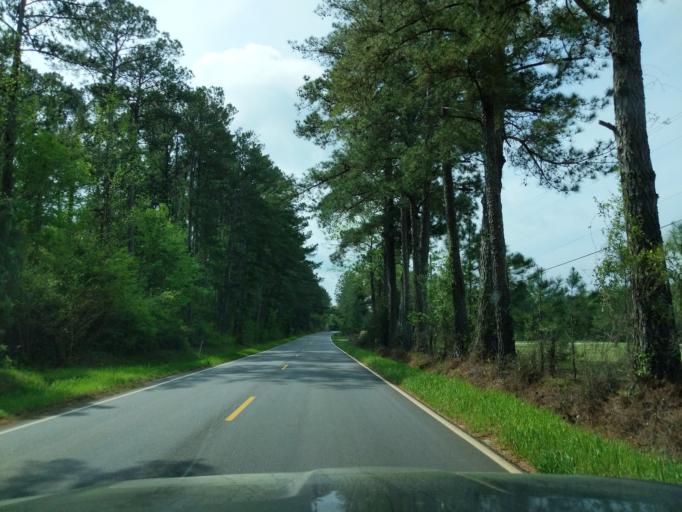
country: US
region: Georgia
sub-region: Columbia County
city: Appling
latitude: 33.6469
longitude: -82.3380
